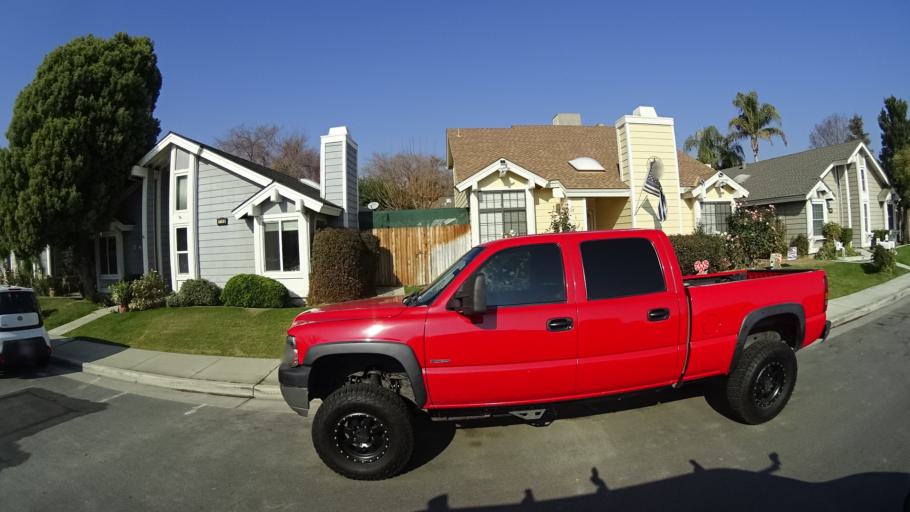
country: US
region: California
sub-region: Kern County
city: Greenacres
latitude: 35.3233
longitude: -119.0828
